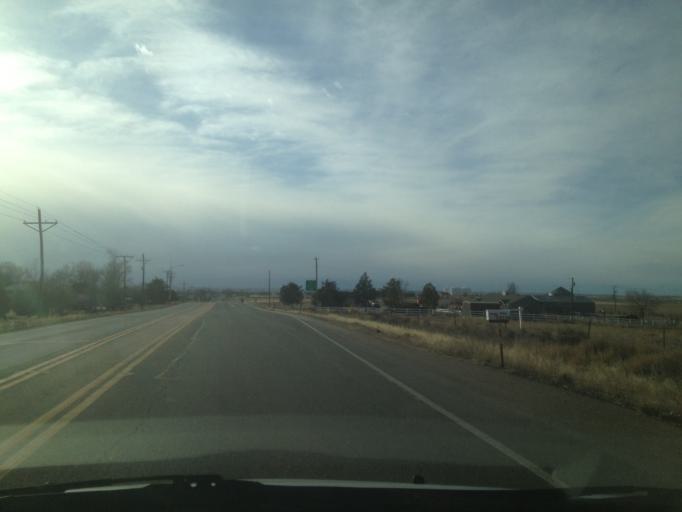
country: US
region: Colorado
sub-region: Weld County
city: Aristocrat Ranchettes
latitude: 40.0803
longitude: -104.7702
